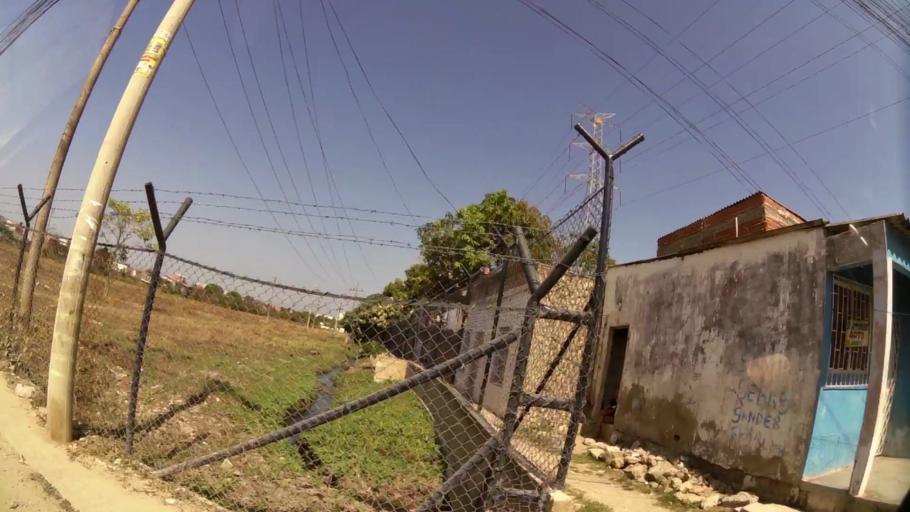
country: CO
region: Bolivar
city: Cartagena
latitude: 10.3759
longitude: -75.4658
